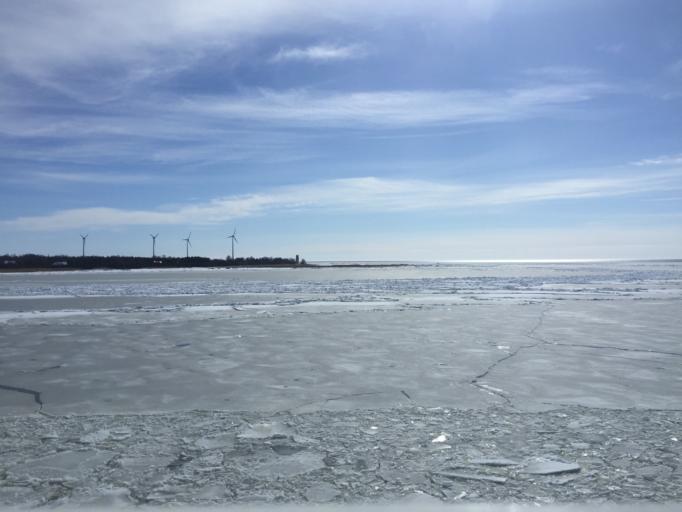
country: EE
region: Laeaene
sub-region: Lihula vald
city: Lihula
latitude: 58.5765
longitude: 23.4993
